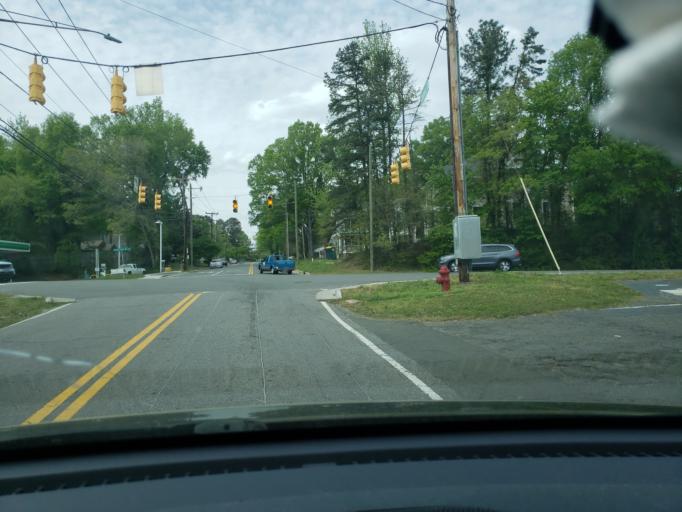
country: US
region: North Carolina
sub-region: Durham County
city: Durham
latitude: 35.9747
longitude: -78.9249
